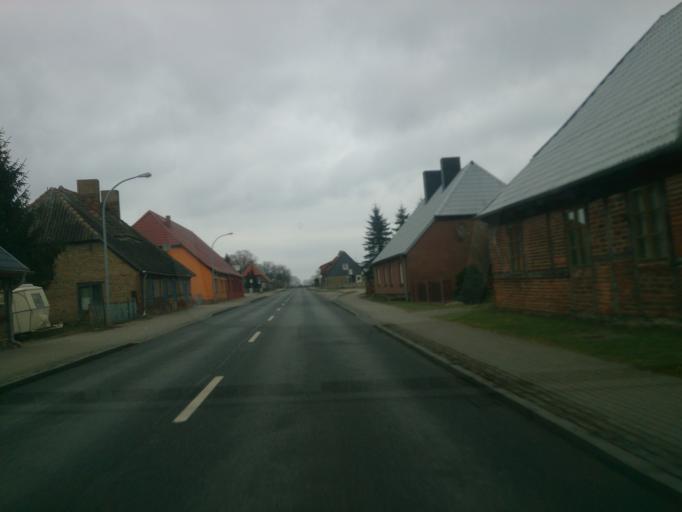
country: DE
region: Mecklenburg-Vorpommern
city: Wackerow
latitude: 53.7233
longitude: 12.9182
